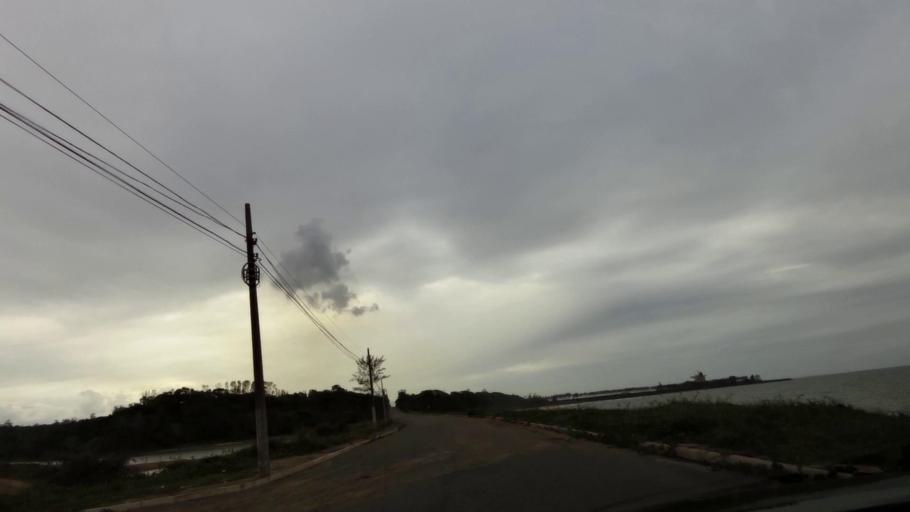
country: BR
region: Espirito Santo
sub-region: Piuma
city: Piuma
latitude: -20.7979
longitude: -40.5827
